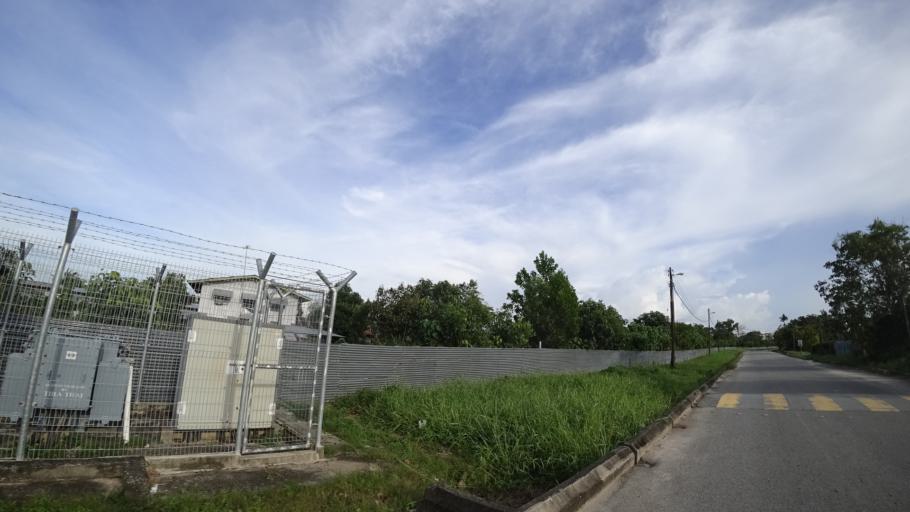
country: BN
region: Brunei and Muara
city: Bandar Seri Begawan
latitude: 4.8236
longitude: 114.8500
